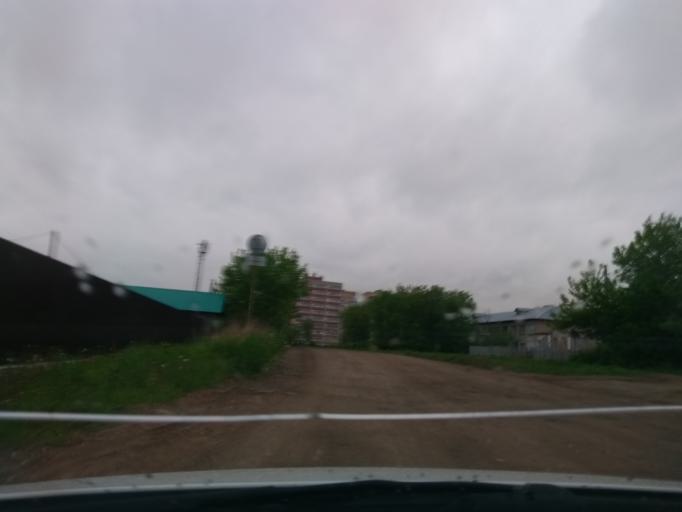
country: RU
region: Perm
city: Froly
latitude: 57.9200
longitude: 56.2684
